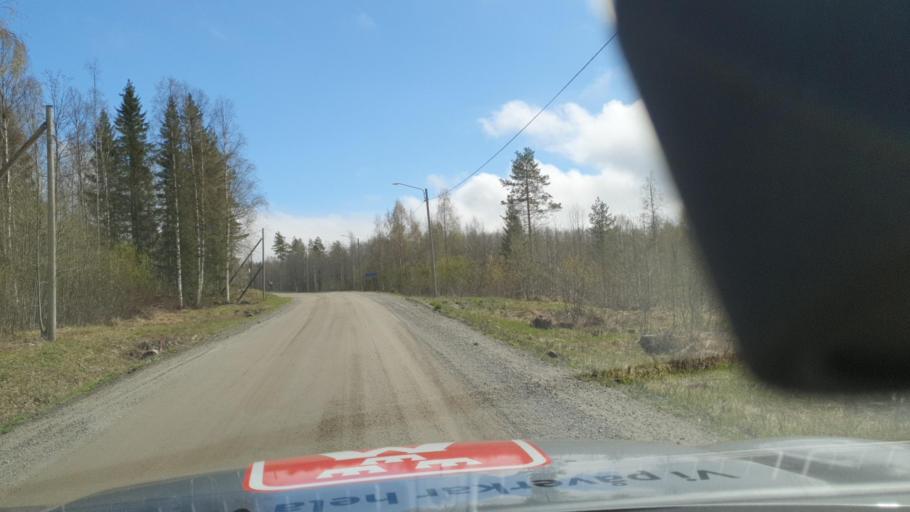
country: SE
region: Vaesterbotten
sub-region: Bjurholms Kommun
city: Bjurholm
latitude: 63.6879
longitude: 18.9595
